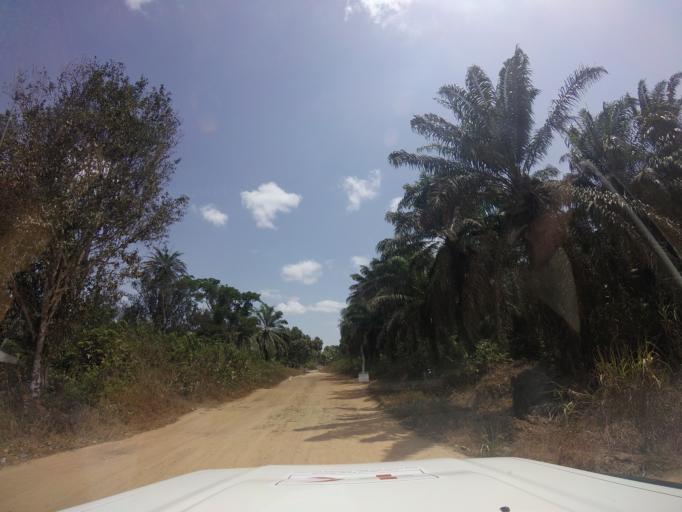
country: SL
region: Southern Province
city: Zimmi
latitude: 7.0619
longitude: -11.2755
